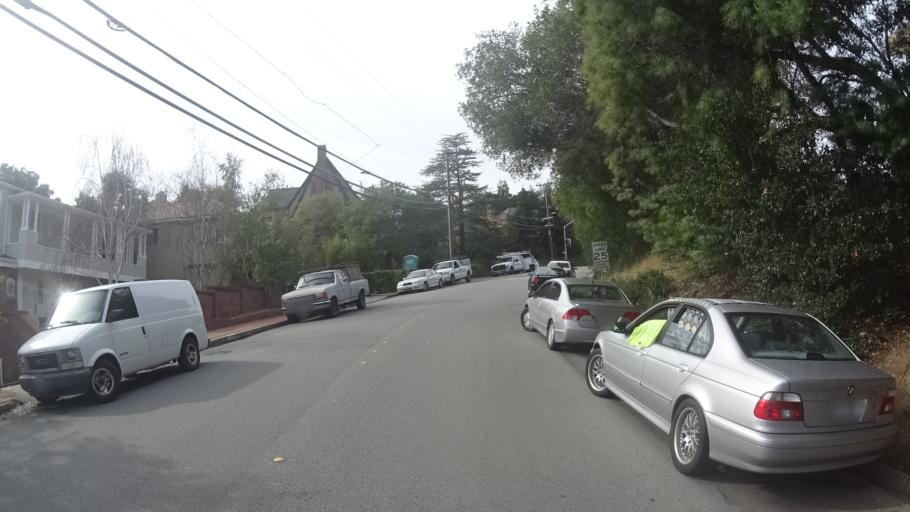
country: US
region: California
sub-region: San Mateo County
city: Hillsborough
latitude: 37.5790
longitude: -122.3829
